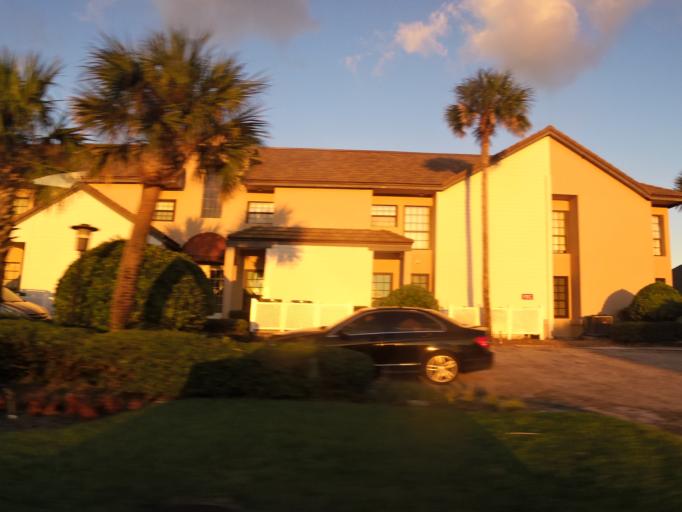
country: US
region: Florida
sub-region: Saint Johns County
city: Sawgrass
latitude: 30.2097
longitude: -81.3696
